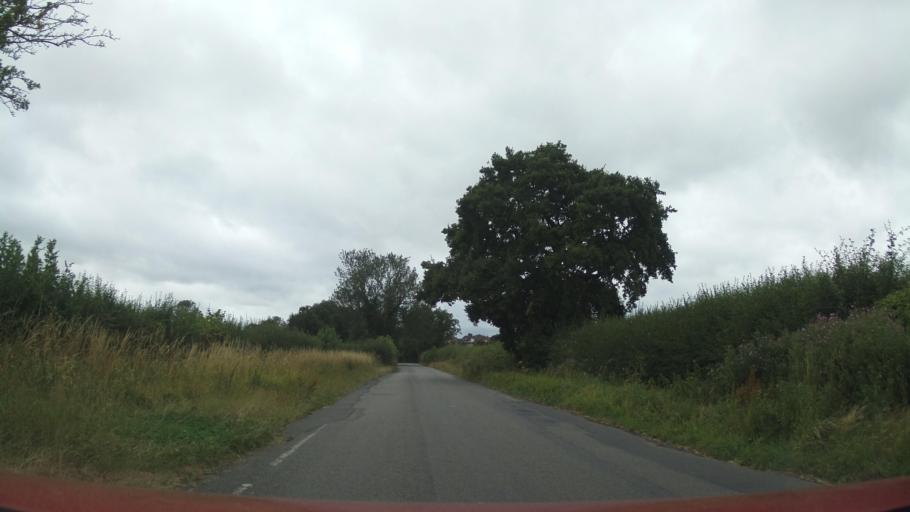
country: GB
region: England
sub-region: Derbyshire
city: Findern
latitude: 52.8765
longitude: -1.5400
